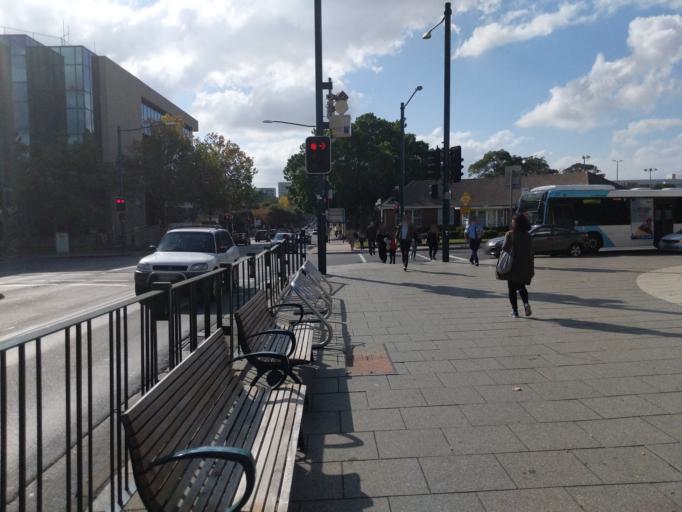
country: AU
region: New South Wales
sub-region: Fairfield
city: Liverpool
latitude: -33.9233
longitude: 150.9269
